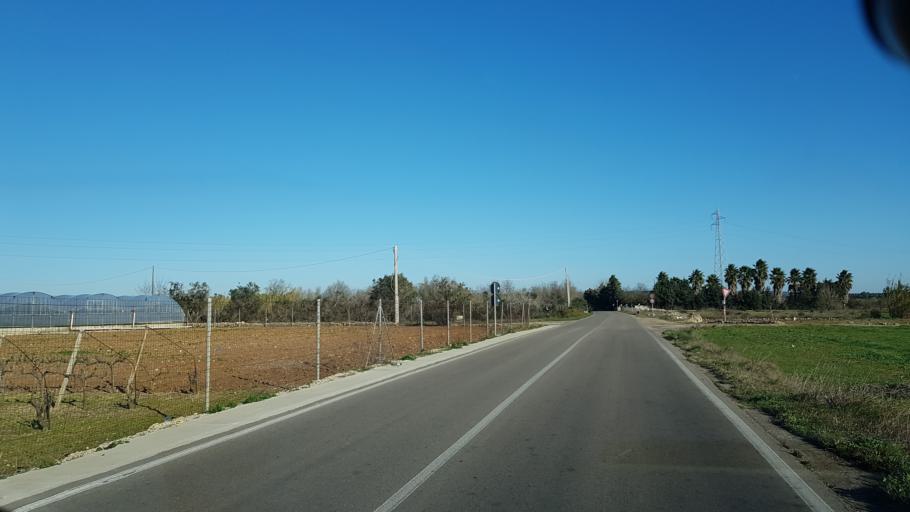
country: IT
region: Apulia
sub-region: Provincia di Lecce
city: Melissano
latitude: 39.9937
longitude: 18.1129
